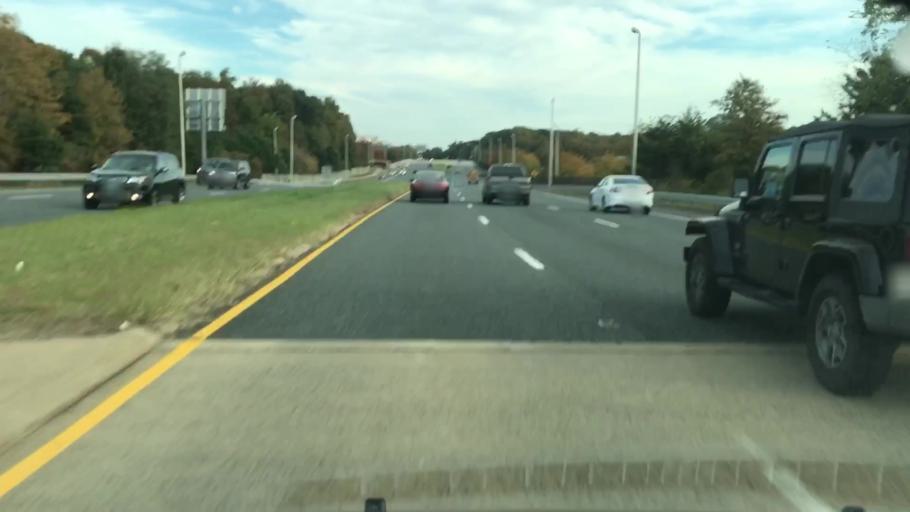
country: US
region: Virginia
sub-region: Fairfax County
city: Springfield
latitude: 38.7690
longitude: -77.1707
